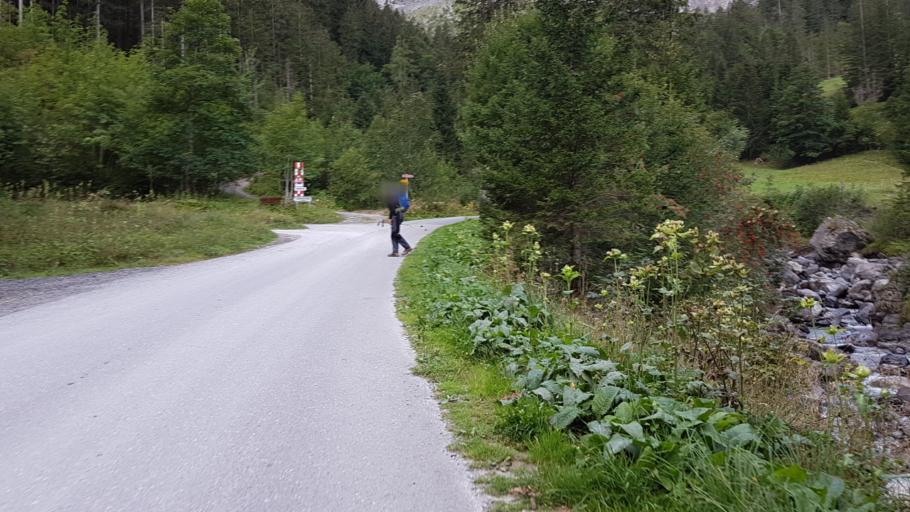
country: CH
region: Bern
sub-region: Frutigen-Niedersimmental District
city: Kandersteg
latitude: 46.4740
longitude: 7.6587
